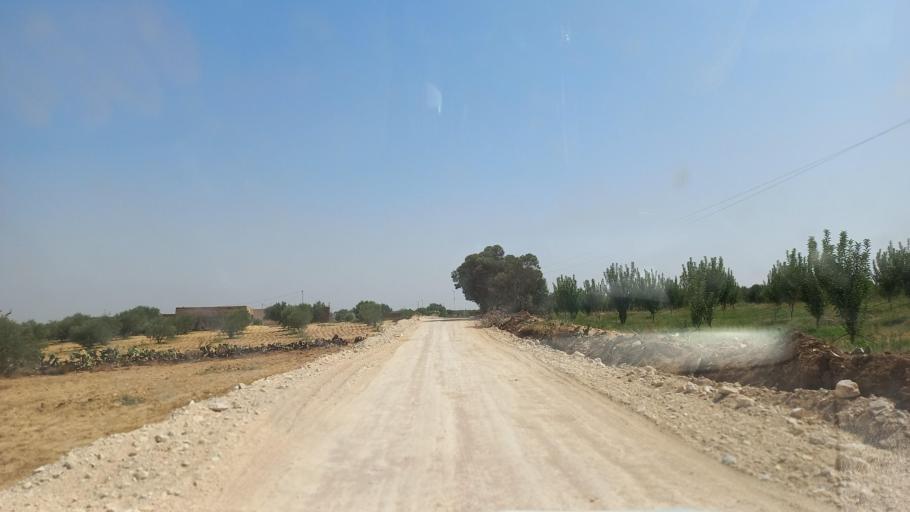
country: TN
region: Al Qasrayn
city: Kasserine
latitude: 35.2617
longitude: 9.0098
